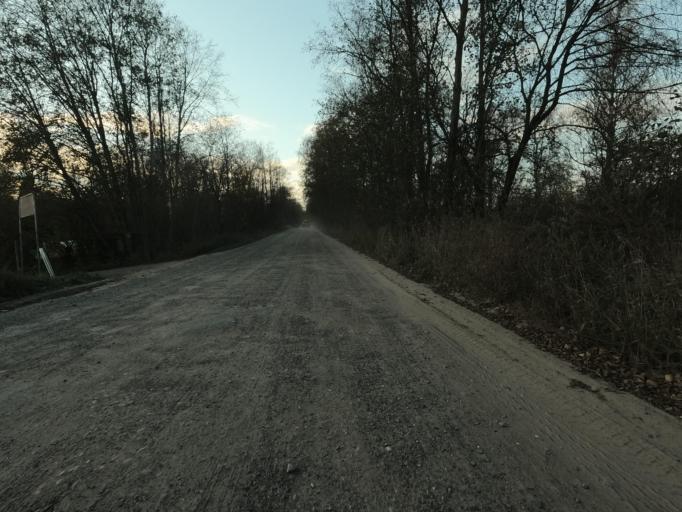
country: RU
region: Leningrad
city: Mga
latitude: 59.7680
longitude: 31.2366
